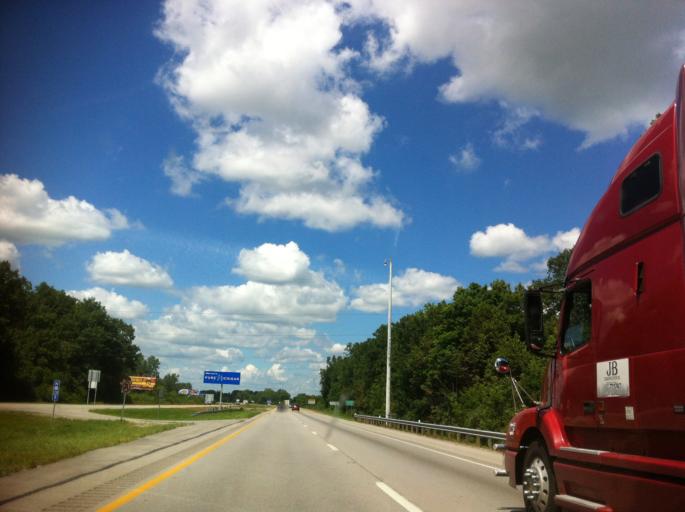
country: US
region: Ohio
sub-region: Lucas County
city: Sylvania
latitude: 41.7251
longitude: -83.6886
